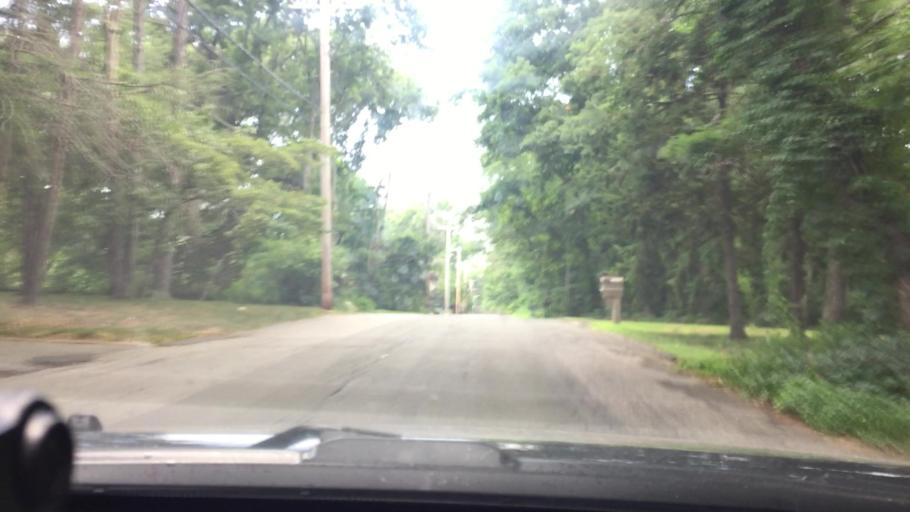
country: US
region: New York
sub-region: Suffolk County
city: Mount Sinai
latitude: 40.9246
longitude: -73.0148
